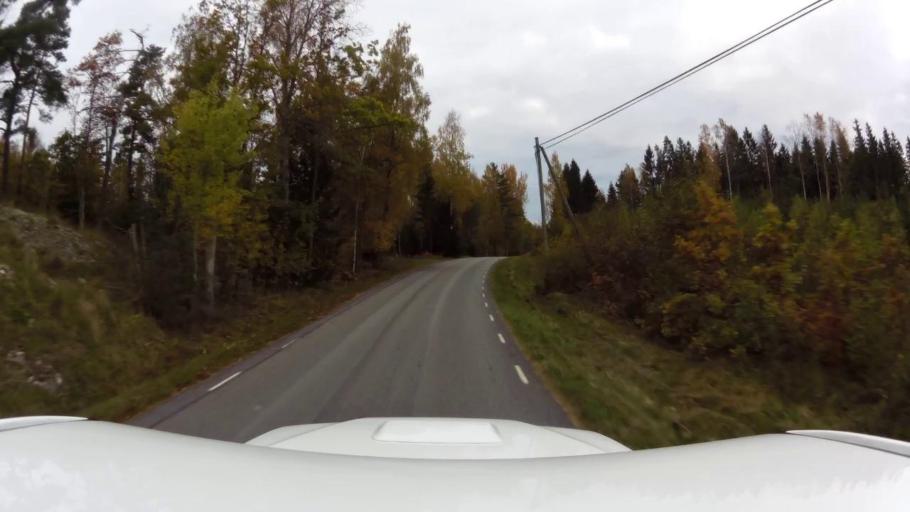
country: SE
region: OEstergoetland
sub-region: Linkopings Kommun
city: Ljungsbro
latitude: 58.5466
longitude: 15.4143
